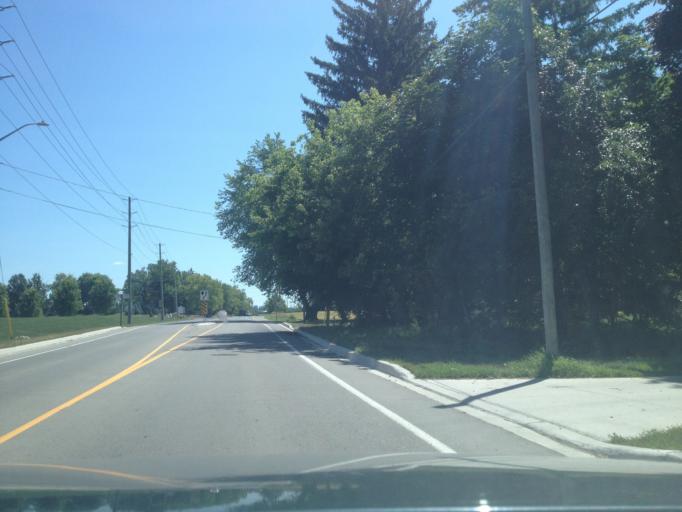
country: CA
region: Ontario
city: Waterloo
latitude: 43.5398
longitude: -80.5105
